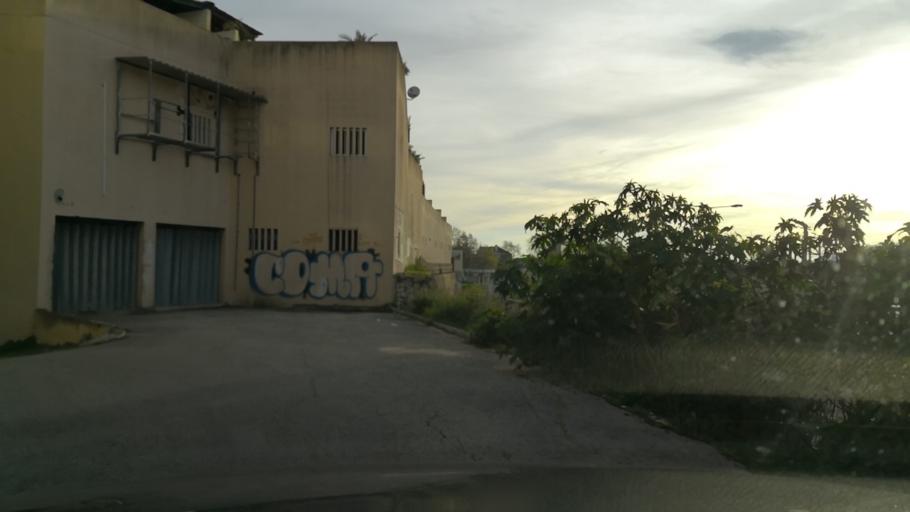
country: PT
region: Setubal
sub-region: Setubal
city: Setubal
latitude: 38.5303
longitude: -8.8845
